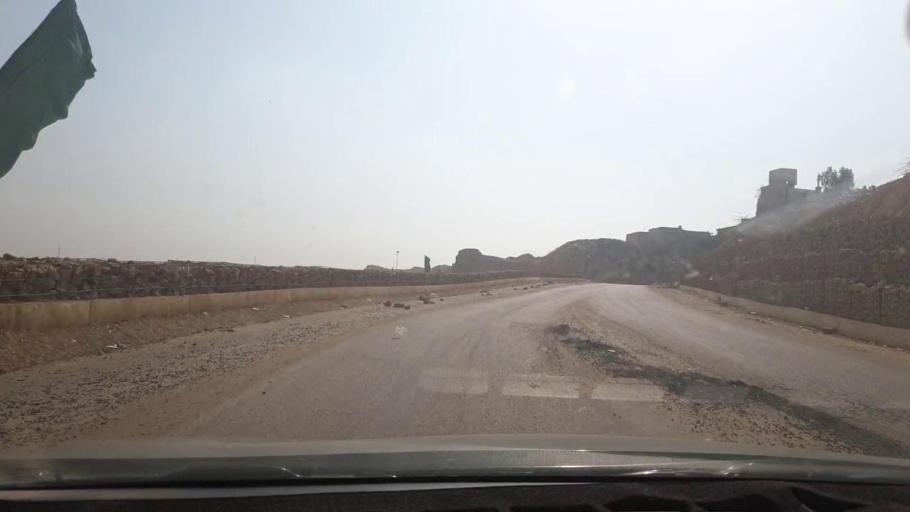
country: PK
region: Sindh
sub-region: Karachi District
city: Karachi
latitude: 24.9728
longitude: 66.9981
